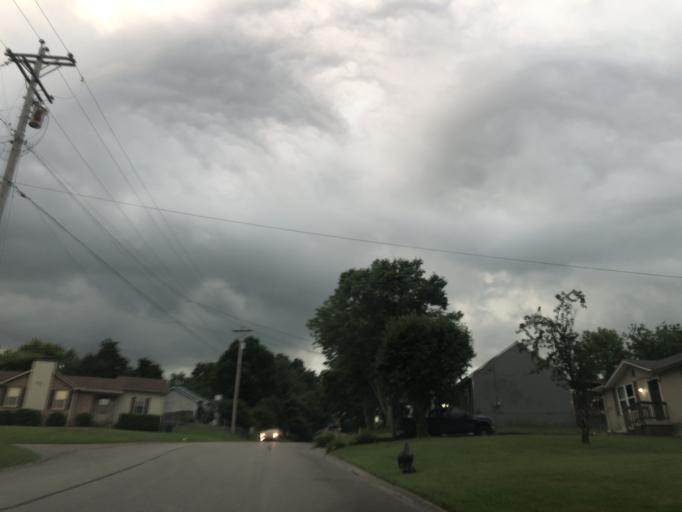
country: US
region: Tennessee
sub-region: Davidson County
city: Lakewood
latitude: 36.1473
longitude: -86.6295
